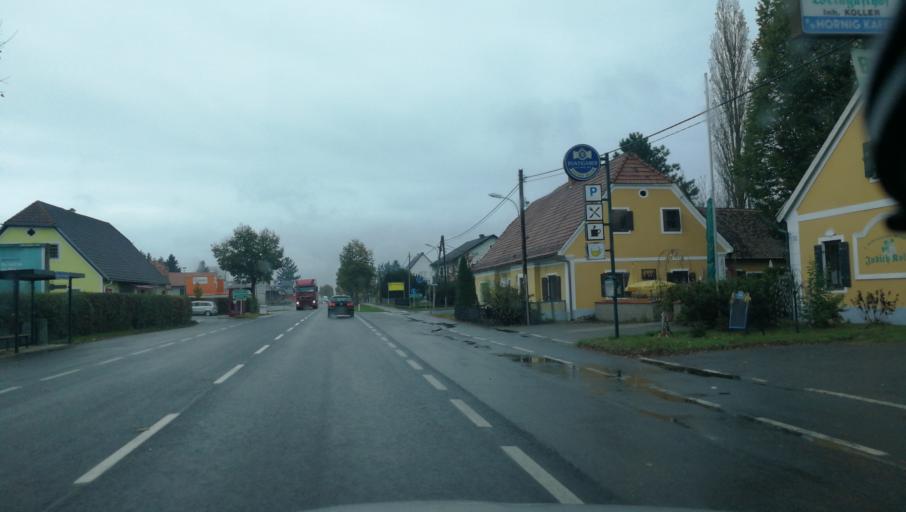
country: AT
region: Styria
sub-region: Politischer Bezirk Leibnitz
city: Sankt Veit am Vogau
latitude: 46.7317
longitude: 15.6135
